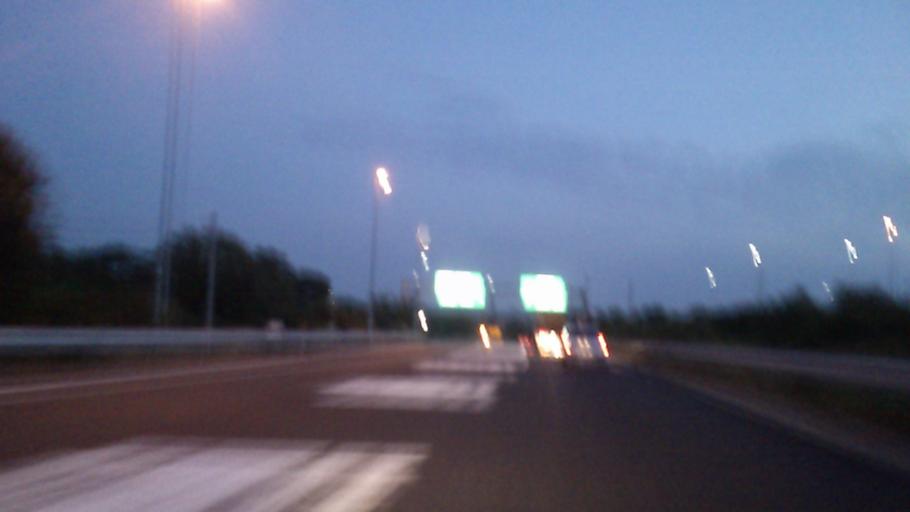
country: JP
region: Aichi
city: Kasugai
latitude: 35.2884
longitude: 136.9809
